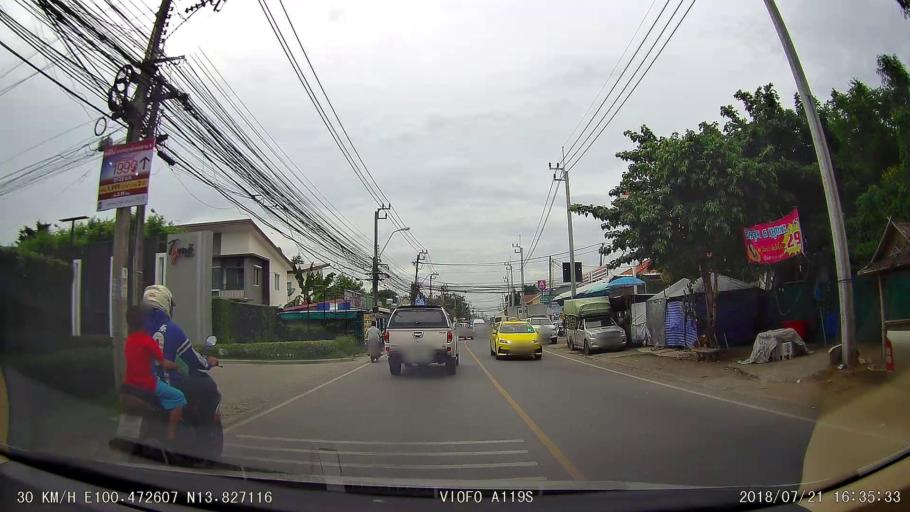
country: TH
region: Nonthaburi
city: Bang Kruai
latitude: 13.8272
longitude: 100.4725
